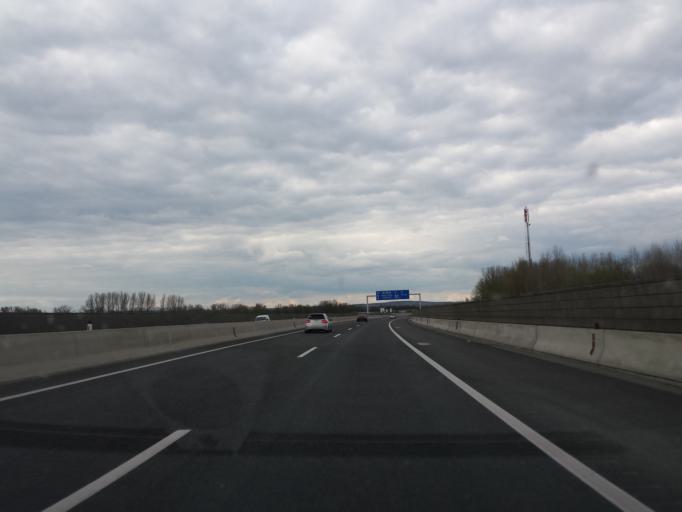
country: AT
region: Lower Austria
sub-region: Politischer Bezirk Krems
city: Grafenegg
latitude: 48.3962
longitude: 15.7335
